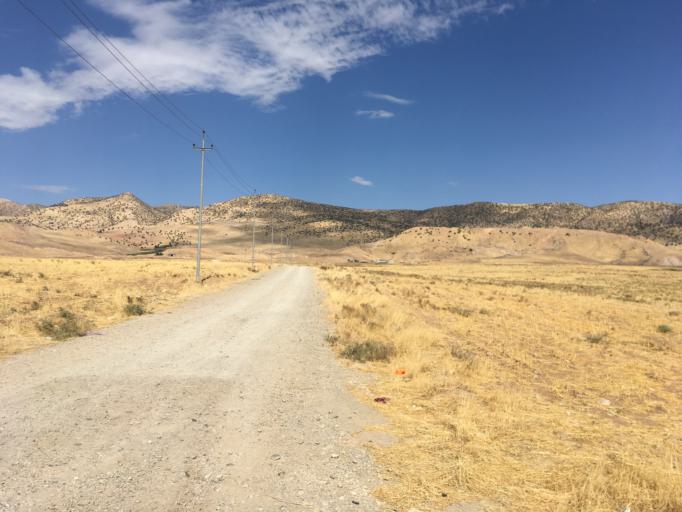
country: IQ
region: Arbil
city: Koysinceq
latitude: 36.1009
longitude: 44.4921
